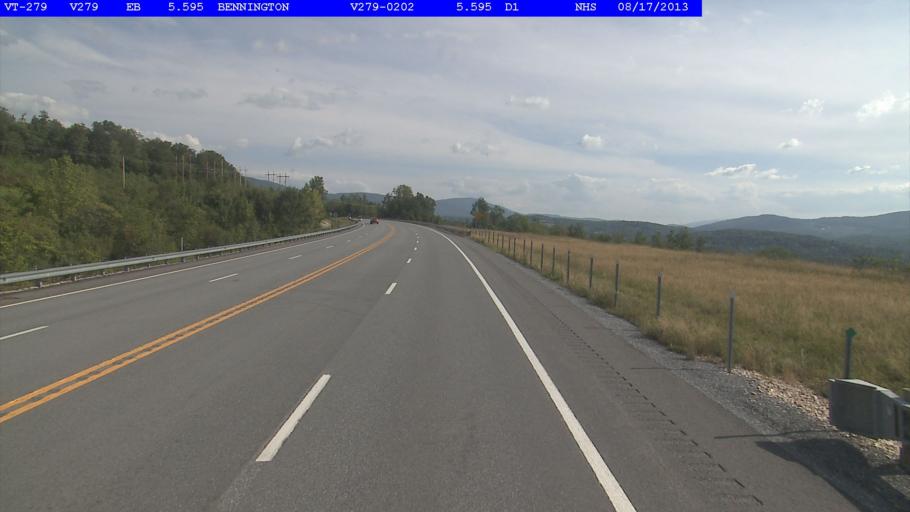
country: US
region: Vermont
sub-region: Bennington County
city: Bennington
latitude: 42.8931
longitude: -73.1768
